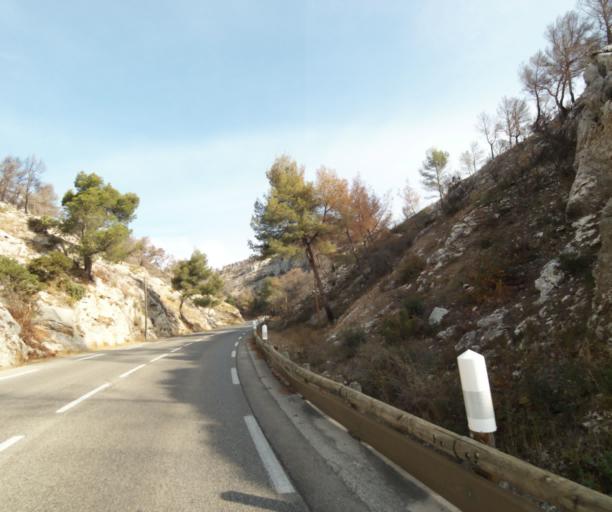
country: FR
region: Provence-Alpes-Cote d'Azur
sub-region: Departement des Bouches-du-Rhone
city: Ensues-la-Redonne
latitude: 43.3419
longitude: 5.1800
